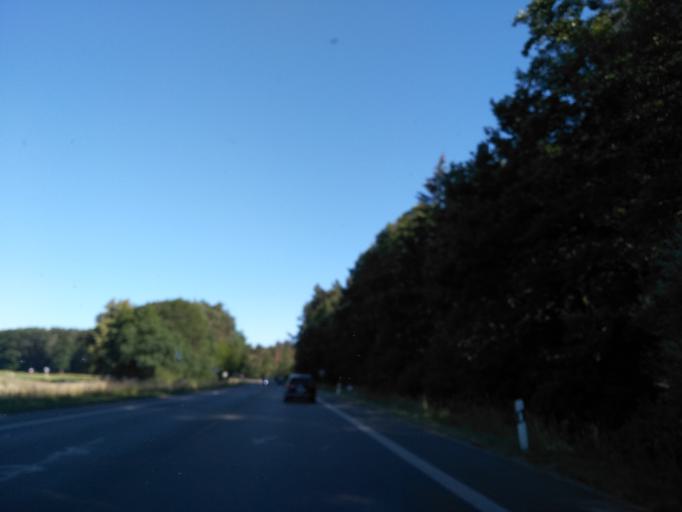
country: DE
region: Bavaria
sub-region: Regierungsbezirk Mittelfranken
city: Hessdorf
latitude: 49.6206
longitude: 10.9507
